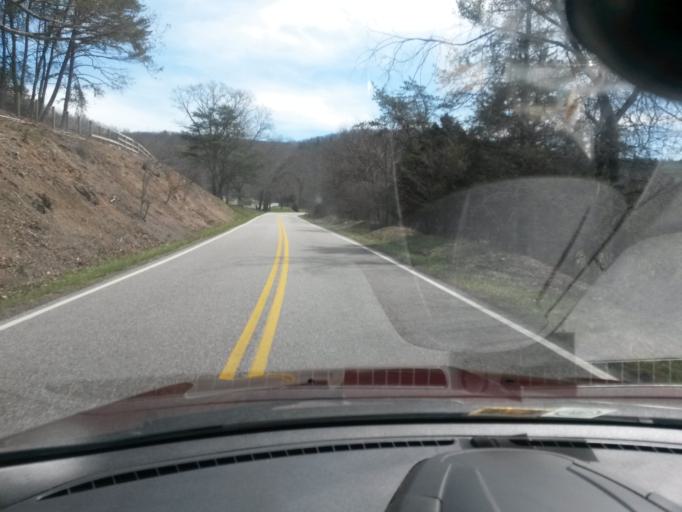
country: US
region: West Virginia
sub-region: Greenbrier County
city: White Sulphur Springs
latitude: 37.6683
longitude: -80.2332
